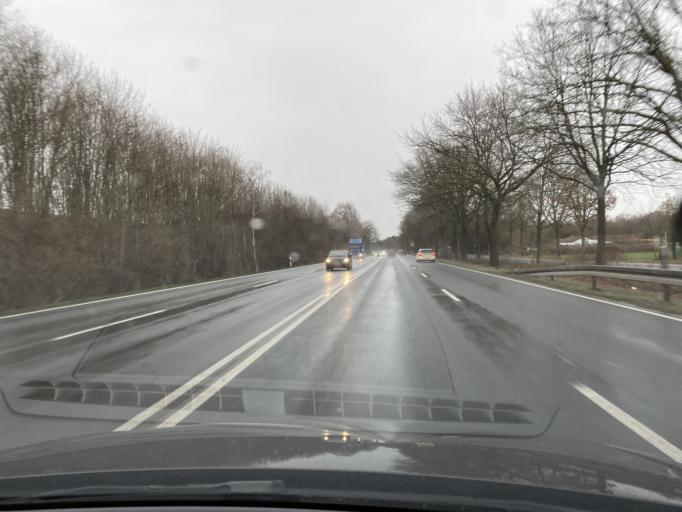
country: DE
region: North Rhine-Westphalia
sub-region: Regierungsbezirk Arnsberg
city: Lippstadt
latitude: 51.6911
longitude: 8.3631
